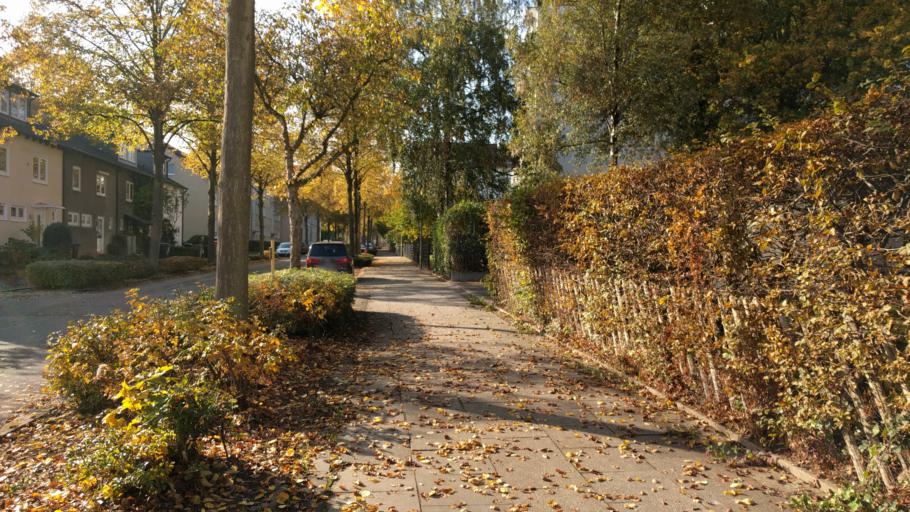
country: DE
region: North Rhine-Westphalia
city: Witten
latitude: 51.4506
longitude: 7.3722
